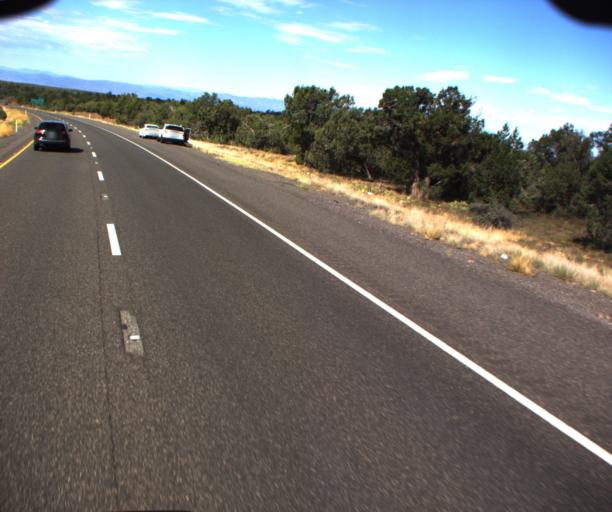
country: US
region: Arizona
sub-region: Yavapai County
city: Village of Oak Creek (Big Park)
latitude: 34.7759
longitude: -111.6354
